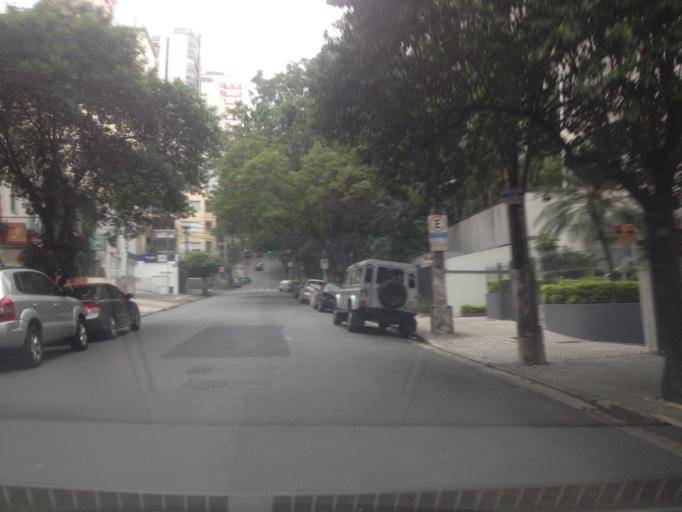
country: BR
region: Sao Paulo
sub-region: Sao Paulo
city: Sao Paulo
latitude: -23.5649
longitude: -46.6629
